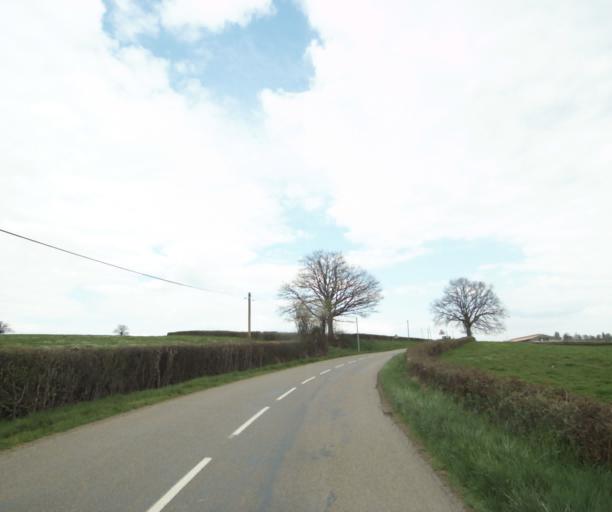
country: FR
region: Bourgogne
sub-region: Departement de Saone-et-Loire
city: Saint-Vallier
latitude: 46.5411
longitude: 4.3754
